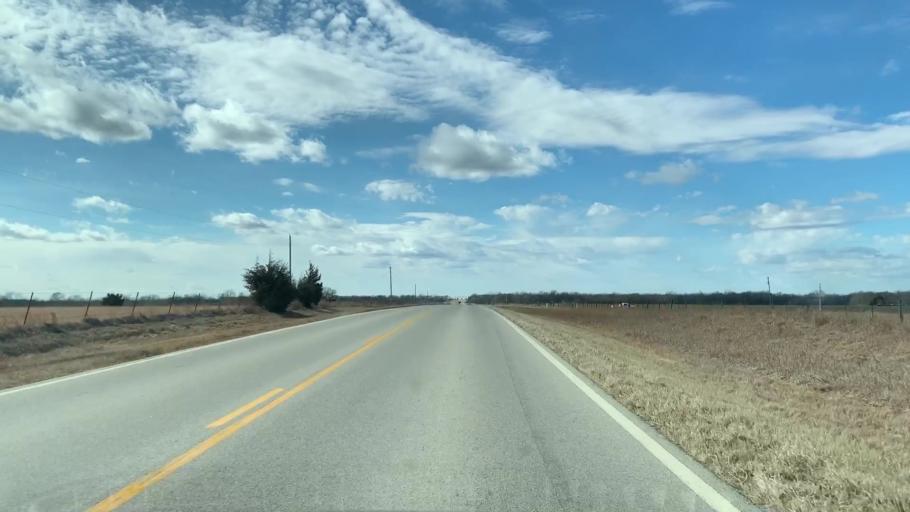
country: US
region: Kansas
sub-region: Neosho County
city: Chanute
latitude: 37.5288
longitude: -95.4500
